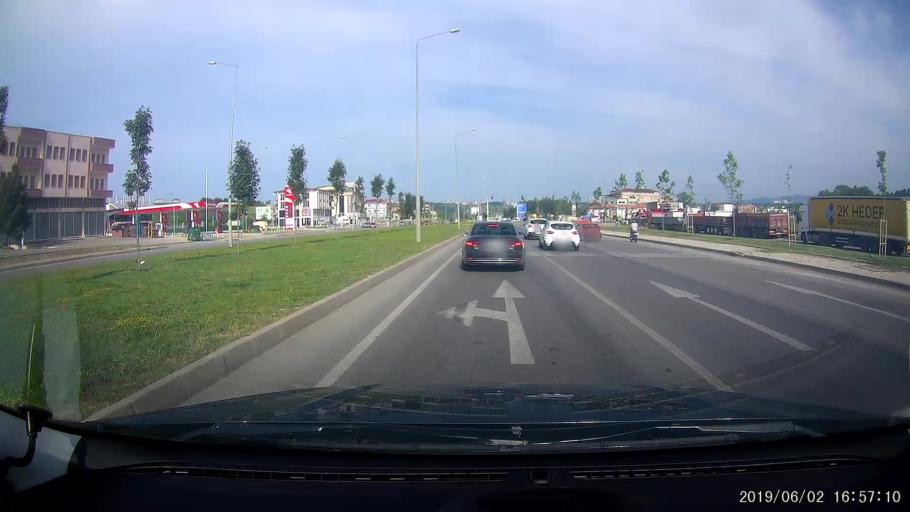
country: TR
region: Samsun
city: Samsun
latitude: 41.2911
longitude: 36.2722
